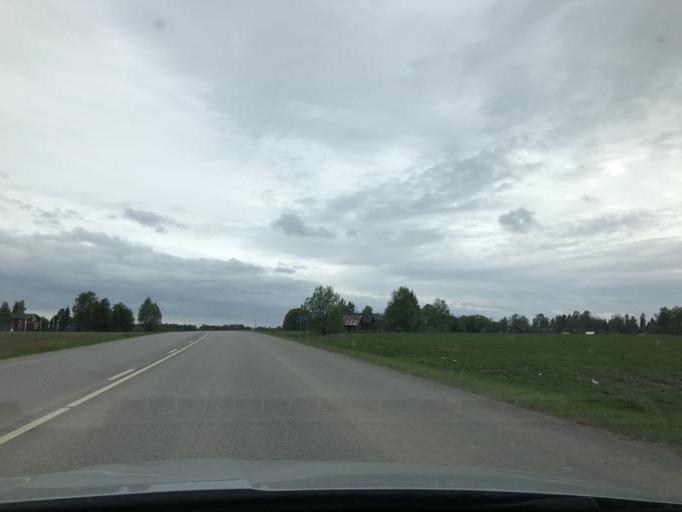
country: SE
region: Norrbotten
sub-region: Pitea Kommun
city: Bergsviken
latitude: 65.3585
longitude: 21.4022
